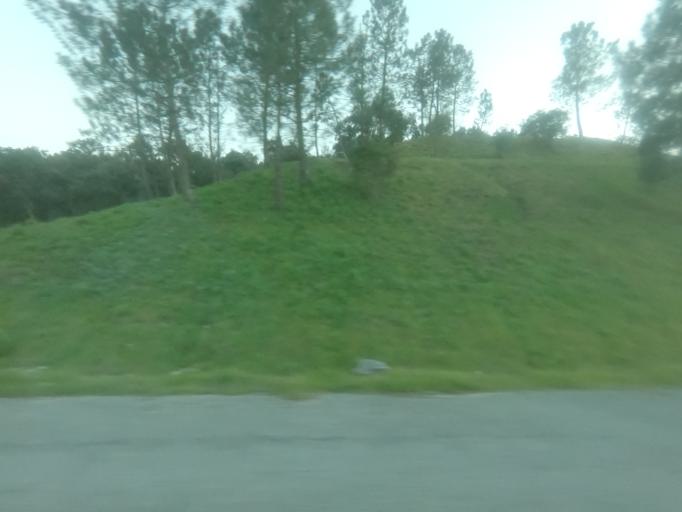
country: PT
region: Leiria
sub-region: Leiria
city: Leiria
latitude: 39.7449
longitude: -8.8333
